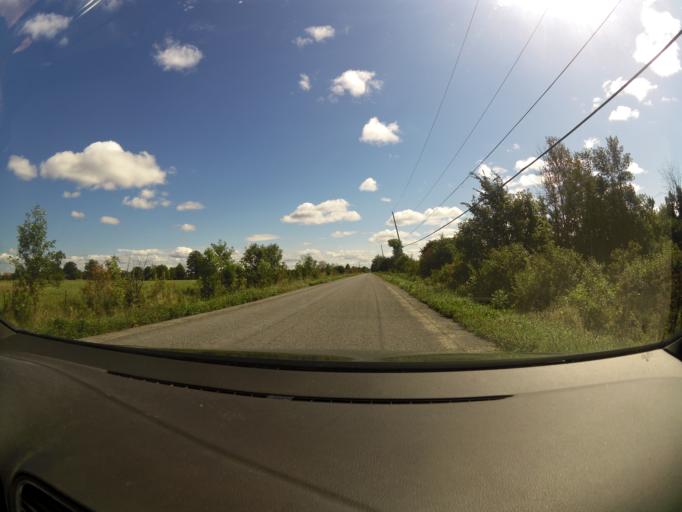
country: CA
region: Ontario
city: Carleton Place
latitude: 45.2272
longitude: -76.1439
